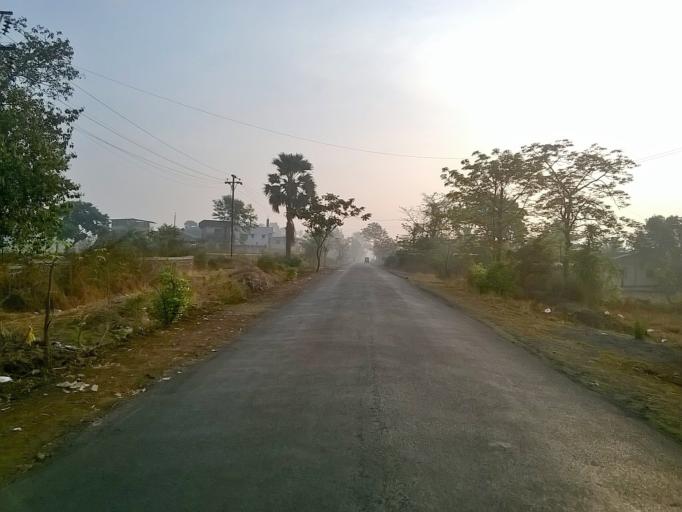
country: IN
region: Maharashtra
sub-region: Raigarh
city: Kalundri
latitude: 19.0075
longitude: 73.1536
